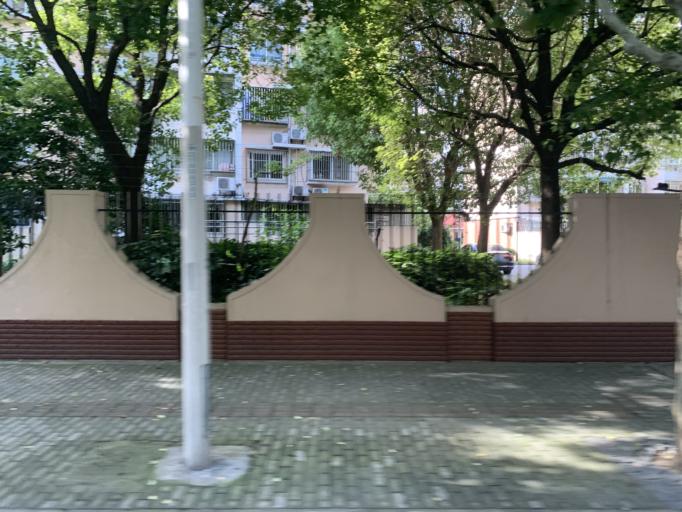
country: CN
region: Shanghai Shi
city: Huamu
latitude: 31.2014
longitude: 121.5369
